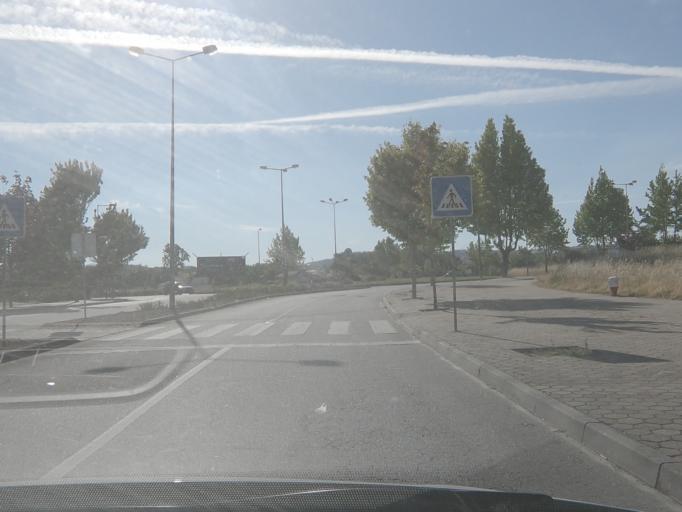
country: PT
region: Viseu
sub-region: Viseu
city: Viseu
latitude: 40.6680
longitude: -7.9014
